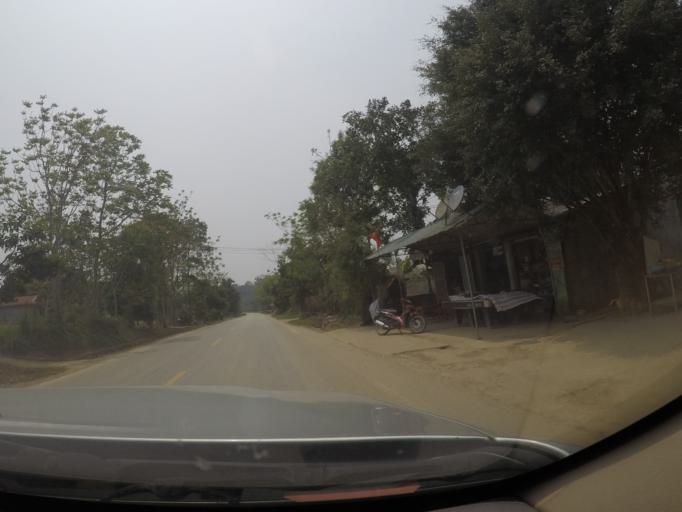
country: VN
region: Thanh Hoa
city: Thi Tran Thuong Xuan
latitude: 19.8554
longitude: 105.4059
